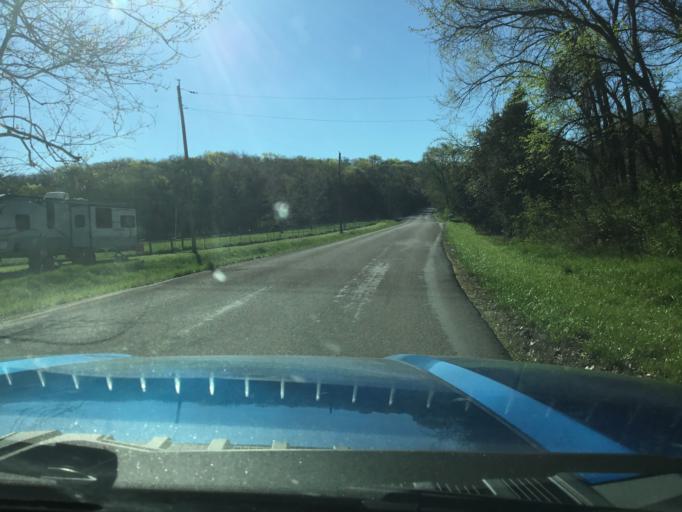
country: US
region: Kansas
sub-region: Douglas County
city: Lawrence
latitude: 38.9928
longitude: -95.2994
